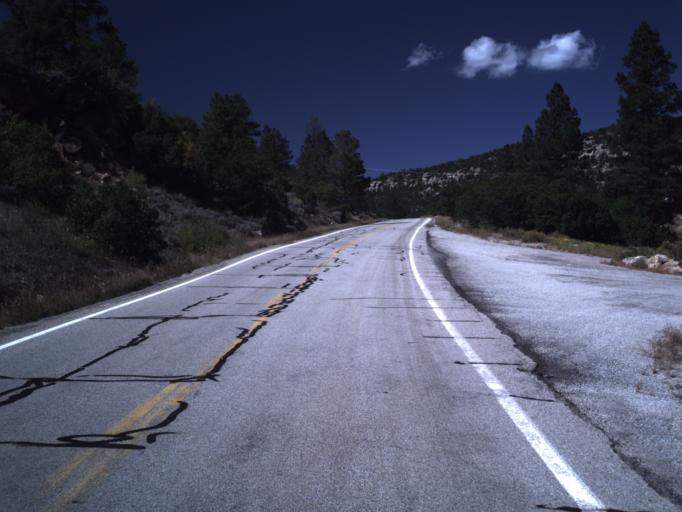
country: US
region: Utah
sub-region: Grand County
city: Moab
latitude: 38.3276
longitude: -109.1108
